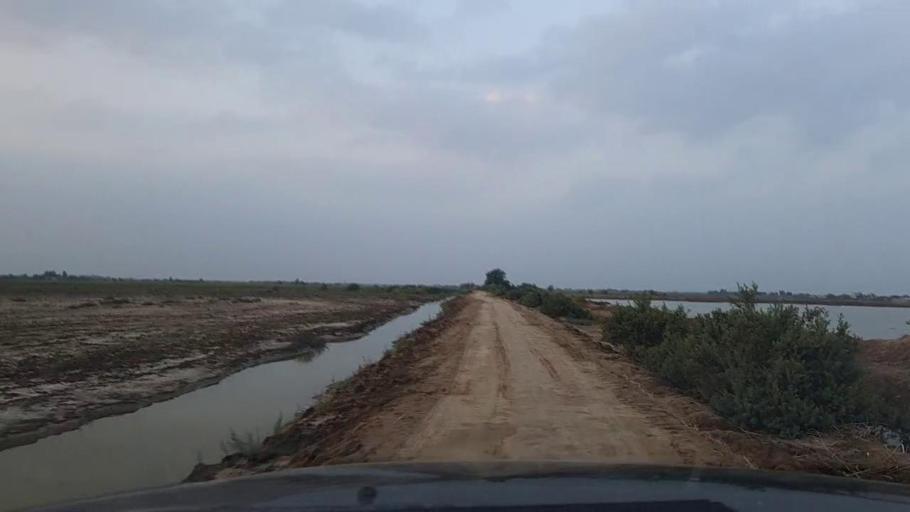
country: PK
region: Sindh
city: Jati
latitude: 24.4952
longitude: 68.3910
